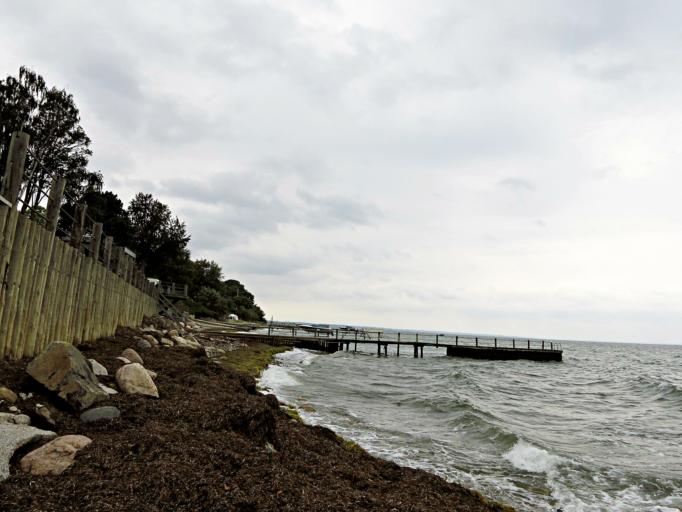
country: DK
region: Capital Region
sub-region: Rudersdal Kommune
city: Trorod
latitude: 55.8638
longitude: 12.5612
